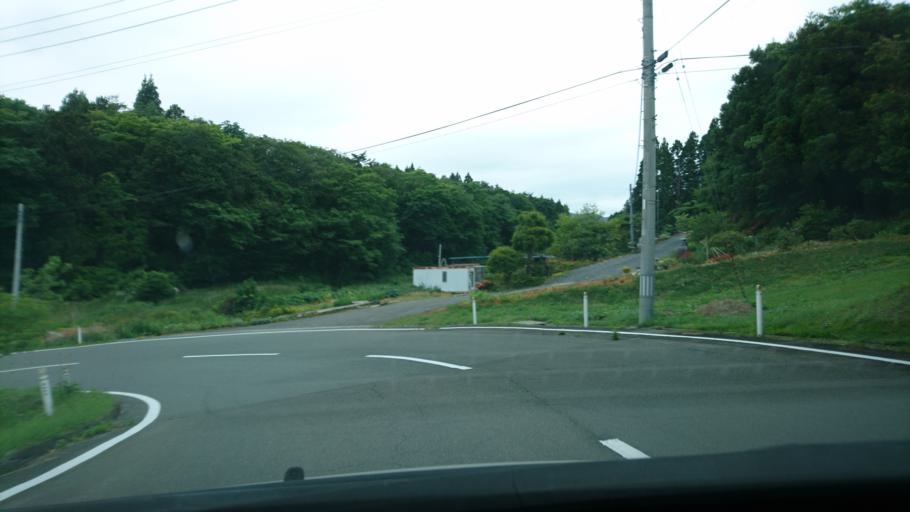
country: JP
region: Miyagi
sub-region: Oshika Gun
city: Onagawa Cho
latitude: 38.7774
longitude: 141.5148
